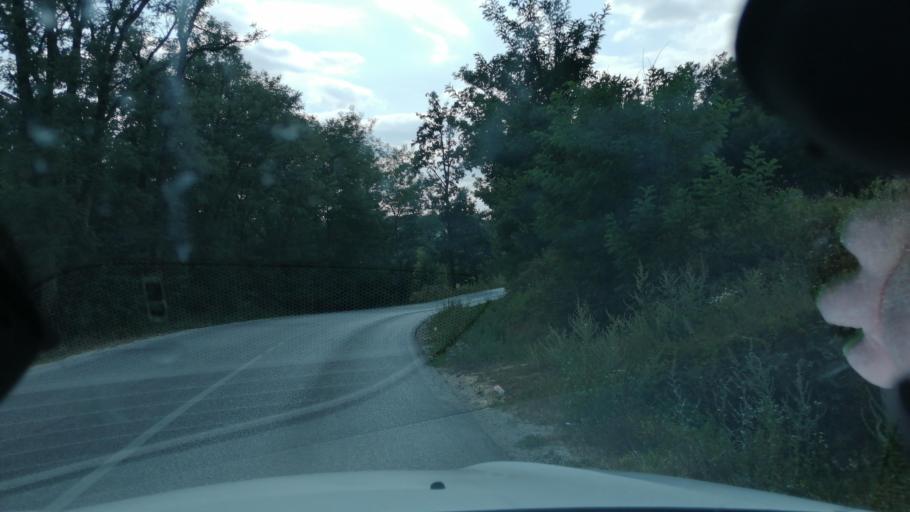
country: RS
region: Central Serbia
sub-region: Moravicki Okrug
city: Cacak
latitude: 43.7998
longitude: 20.2586
